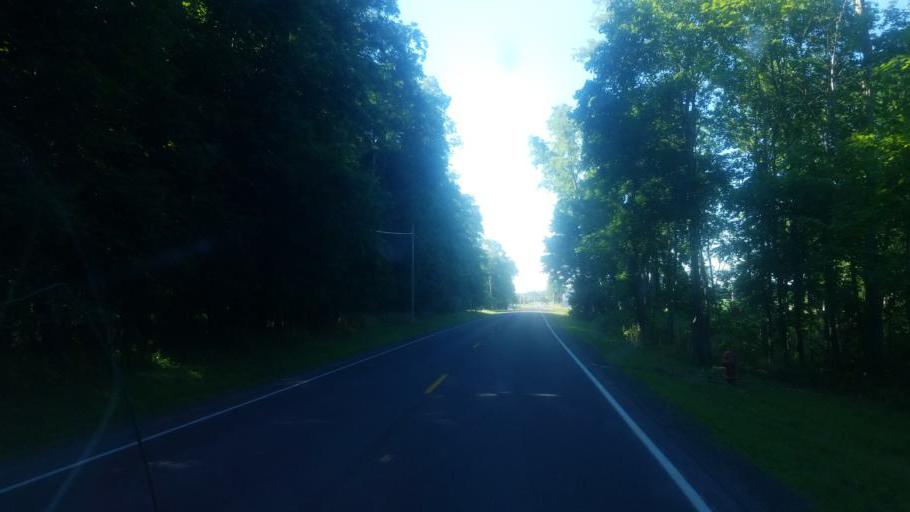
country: US
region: New York
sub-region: Ontario County
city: Phelps
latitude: 42.9201
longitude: -77.0641
